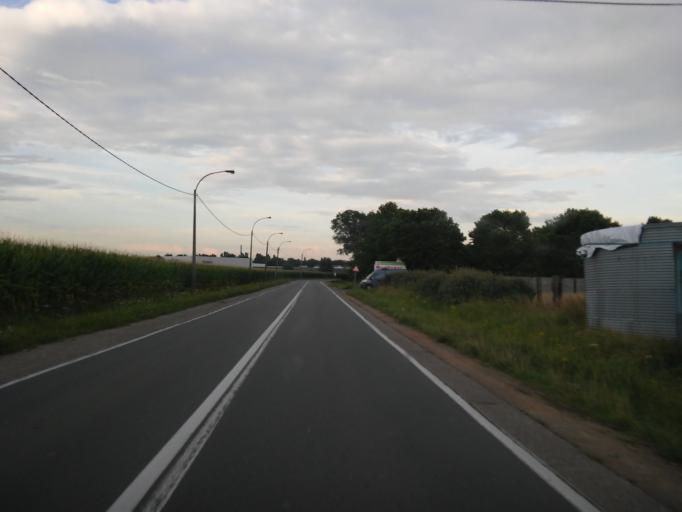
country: BE
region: Flanders
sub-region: Provincie Antwerpen
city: Kontich
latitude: 51.1213
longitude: 4.4213
